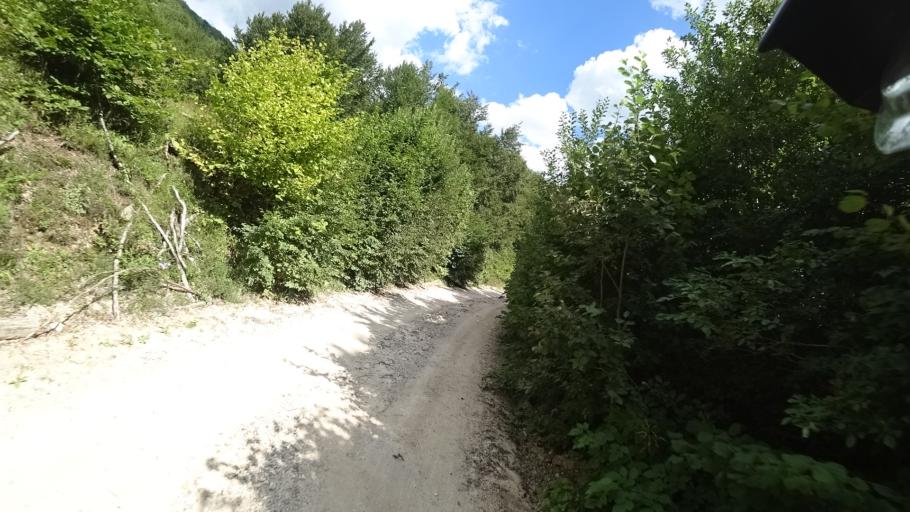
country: BA
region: Federation of Bosnia and Herzegovina
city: Orasac
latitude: 44.5701
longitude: 15.8457
